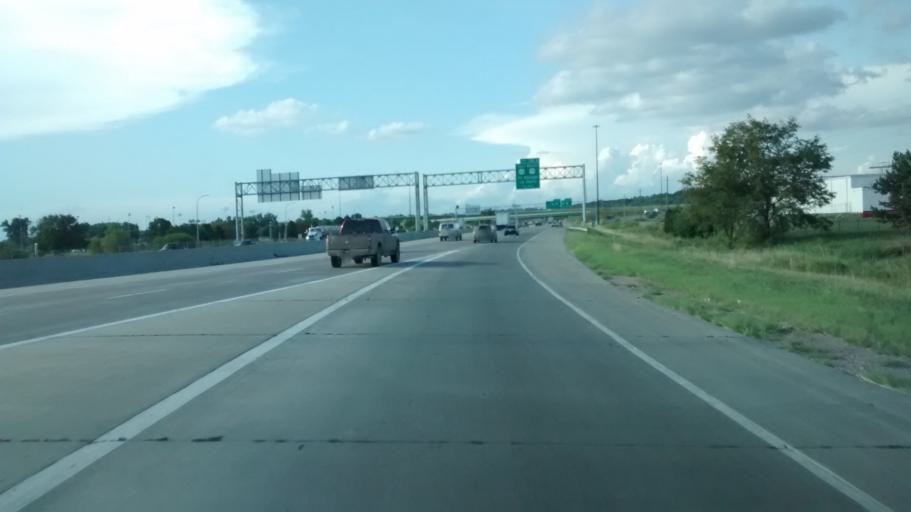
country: US
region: Iowa
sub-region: Woodbury County
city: Sergeant Bluff
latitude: 42.4378
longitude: -96.3751
